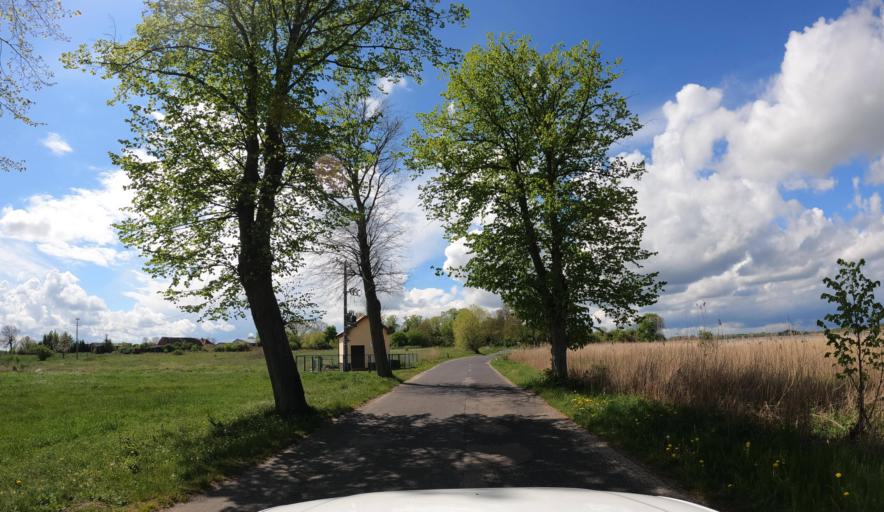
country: PL
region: West Pomeranian Voivodeship
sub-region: Powiat kamienski
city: Wolin
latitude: 53.9078
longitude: 14.6767
